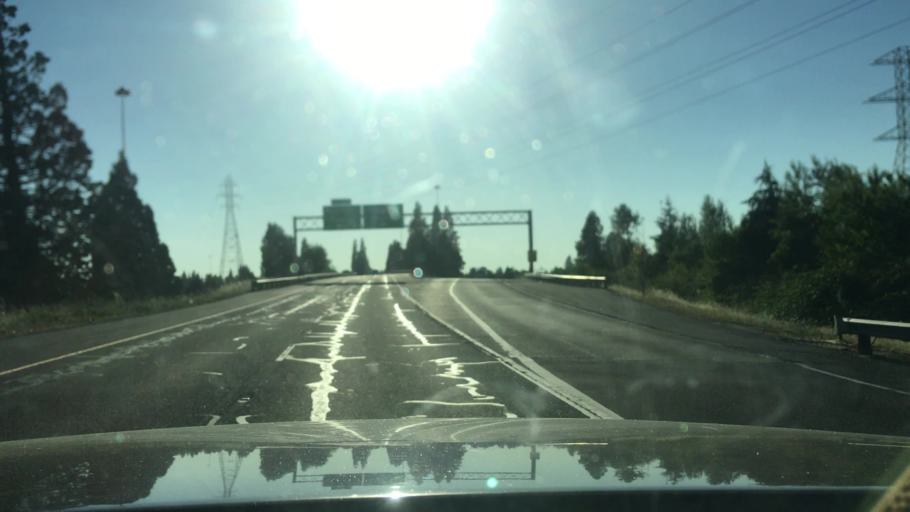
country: US
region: Oregon
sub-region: Lane County
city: Springfield
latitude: 44.0633
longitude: -123.0428
